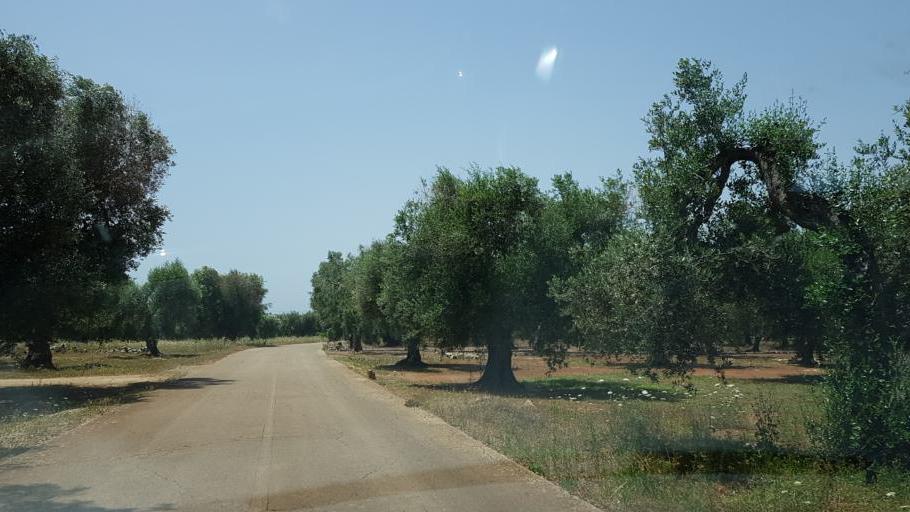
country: IT
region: Apulia
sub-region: Provincia di Lecce
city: Porto Cesareo
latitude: 40.3238
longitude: 17.8865
